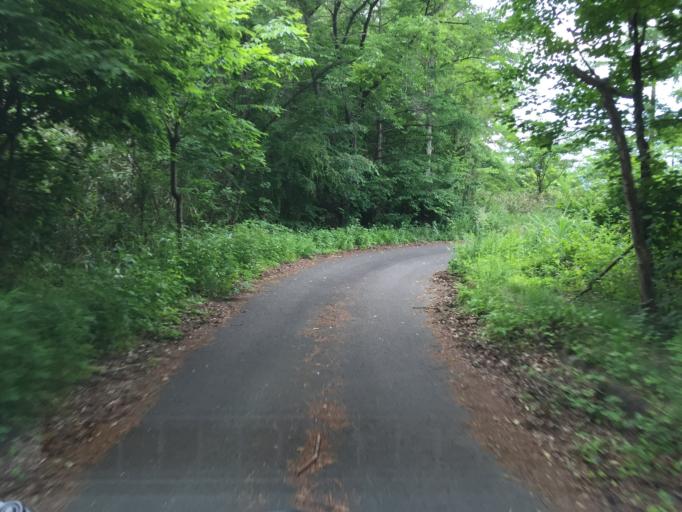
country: JP
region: Fukushima
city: Fukushima-shi
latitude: 37.7199
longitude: 140.3375
